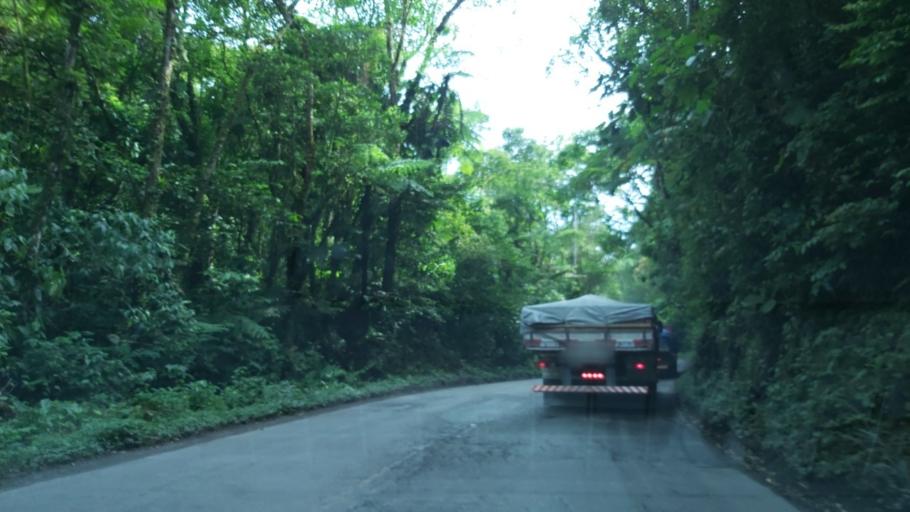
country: BR
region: Sao Paulo
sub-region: Miracatu
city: Miracatu
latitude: -24.0338
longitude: -47.5615
